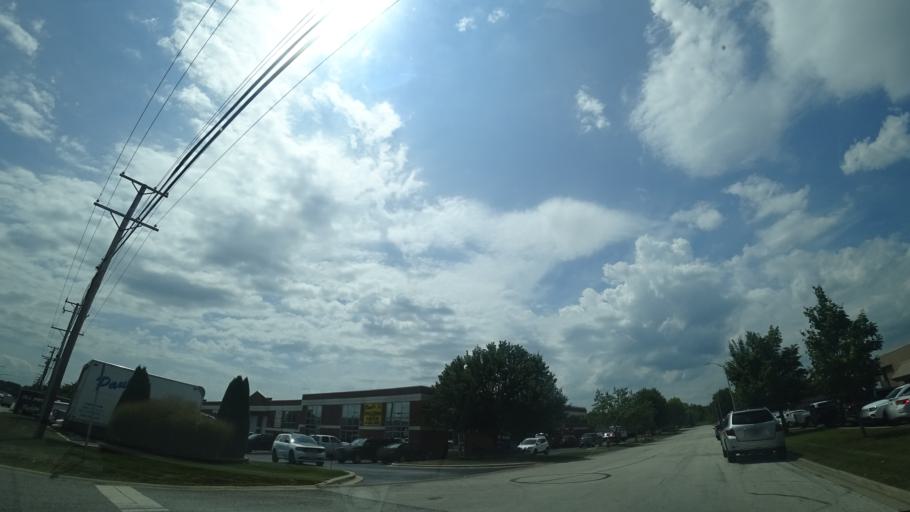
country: US
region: Illinois
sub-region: Cook County
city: Crestwood
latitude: 41.6752
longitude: -87.7586
